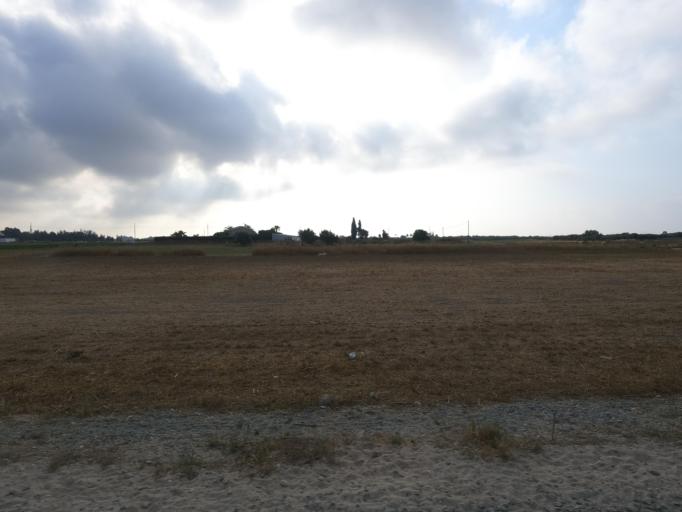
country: CY
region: Larnaka
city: Kiti
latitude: 34.8324
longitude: 33.5559
